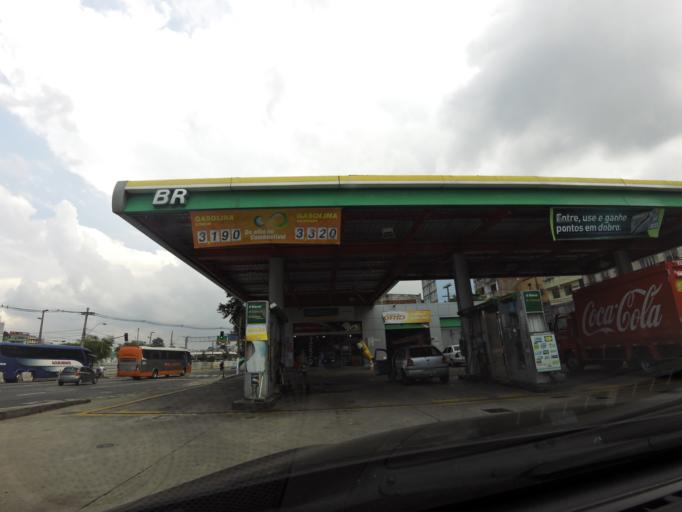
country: BR
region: Espirito Santo
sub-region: Vitoria
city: Vitoria
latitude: -20.3193
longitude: -40.3479
